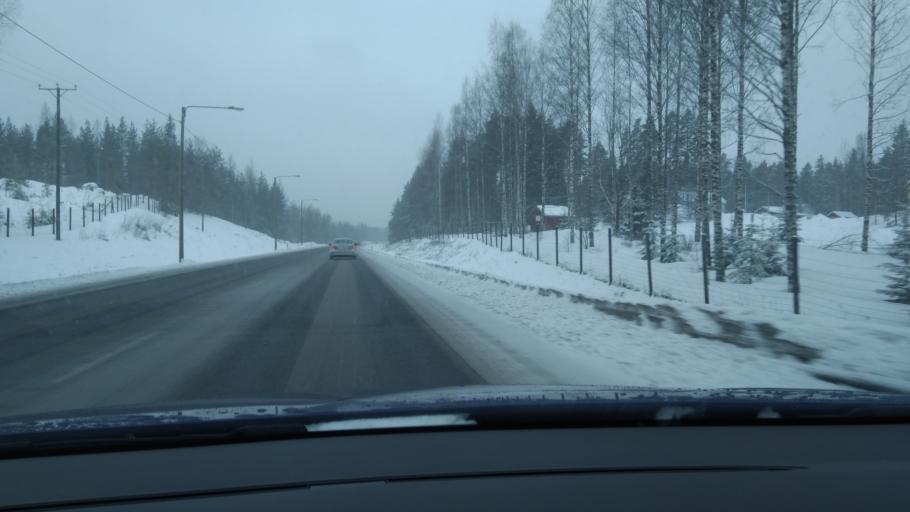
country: FI
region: Pirkanmaa
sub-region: Tampere
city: Kangasala
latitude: 61.5408
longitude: 24.0230
